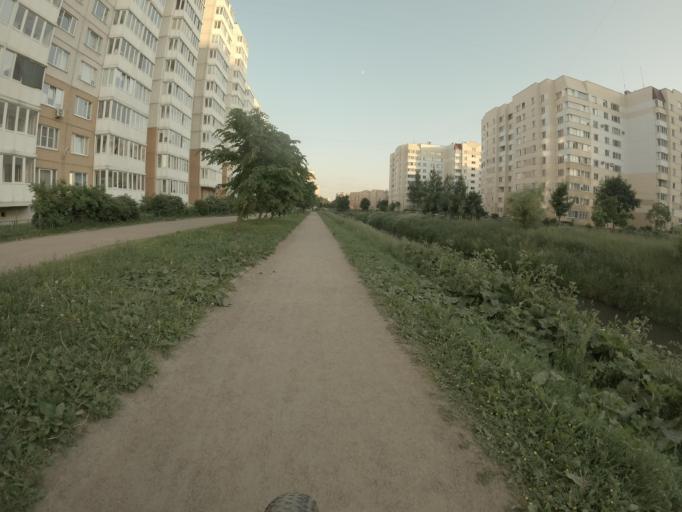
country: RU
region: St.-Petersburg
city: Dachnoye
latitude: 59.8501
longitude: 30.2466
